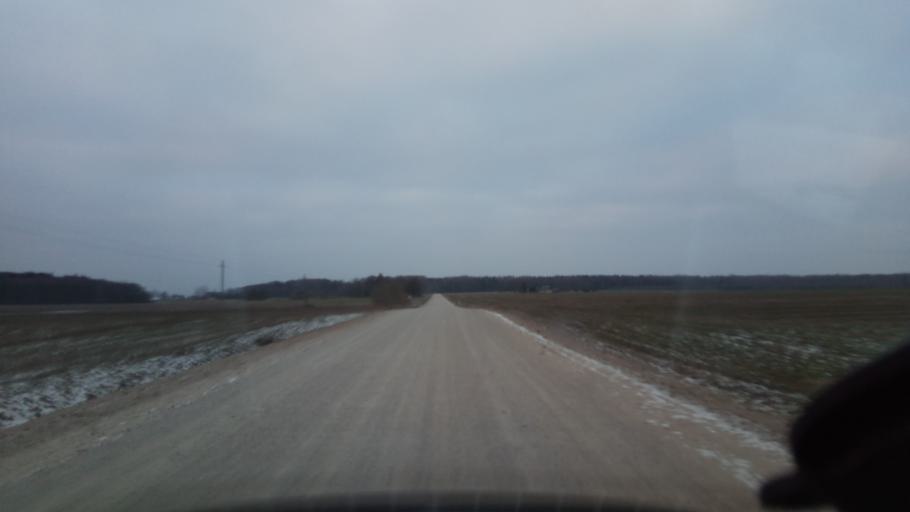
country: LT
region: Alytaus apskritis
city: Varena
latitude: 54.1170
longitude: 24.7407
